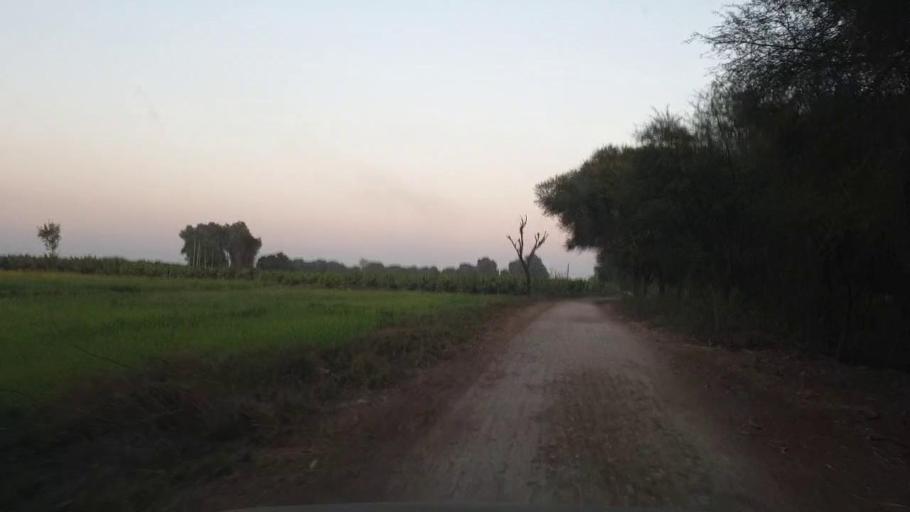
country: PK
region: Sindh
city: Chambar
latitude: 25.3413
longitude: 68.7549
